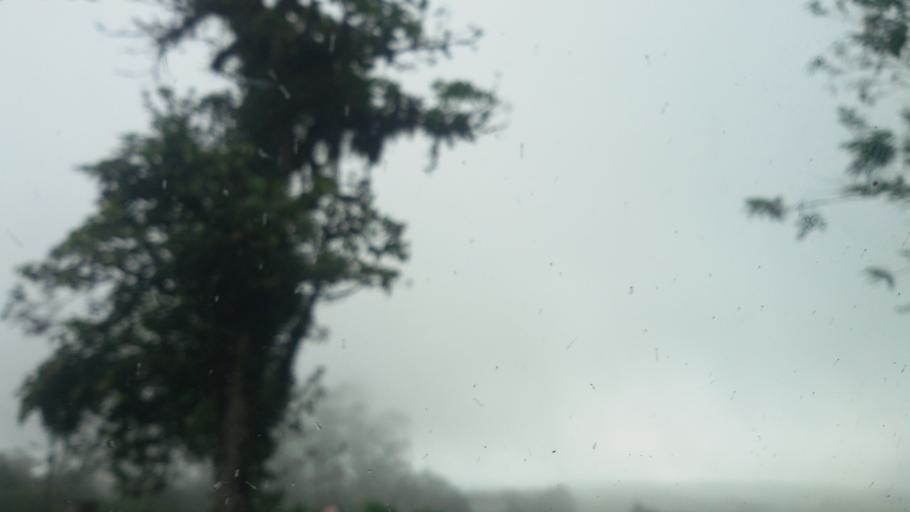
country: CR
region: San Jose
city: Ipis
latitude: 10.0055
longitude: -83.9588
